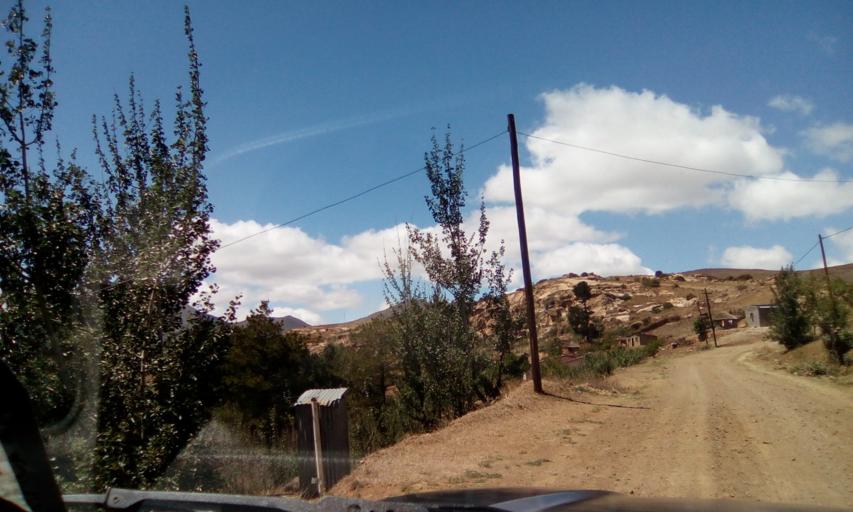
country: LS
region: Qacha's Nek
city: Qacha's Nek
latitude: -30.0677
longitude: 28.6323
